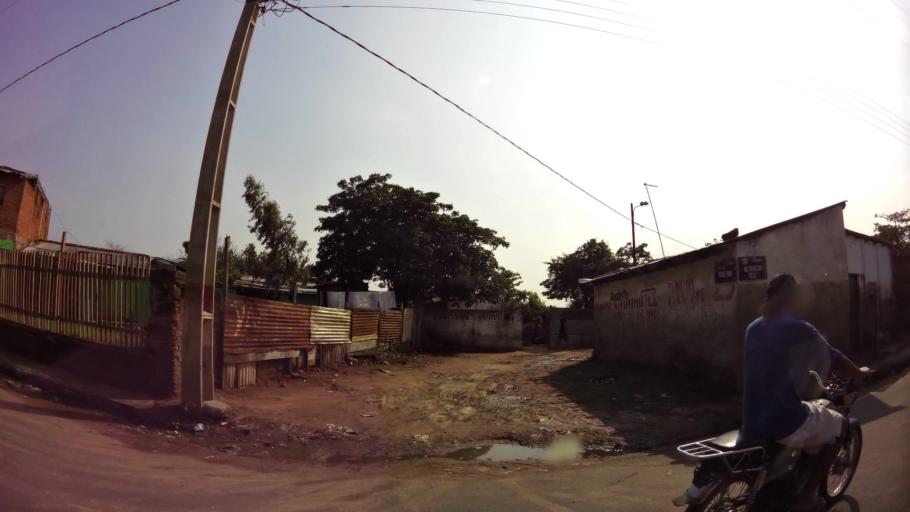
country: PY
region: Asuncion
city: Asuncion
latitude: -25.3095
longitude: -57.6674
